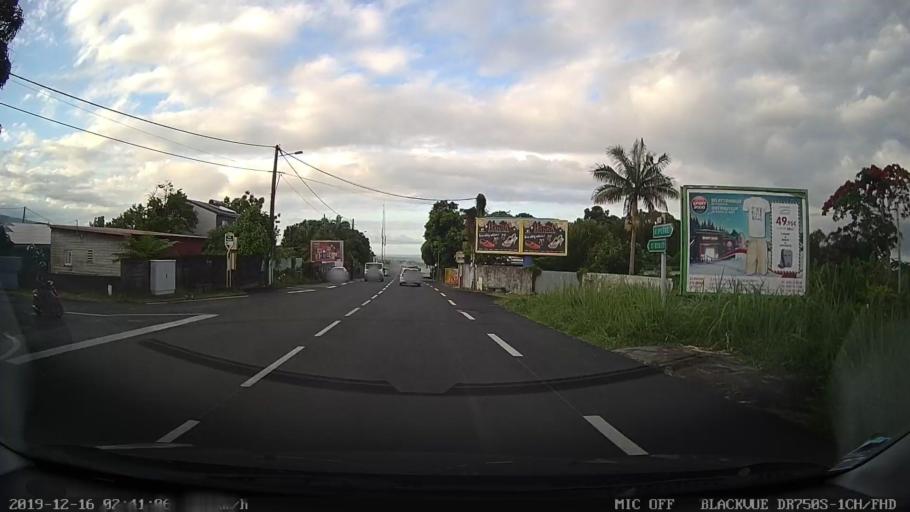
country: RE
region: Reunion
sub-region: Reunion
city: Saint-Benoit
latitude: -21.0690
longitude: 55.7048
